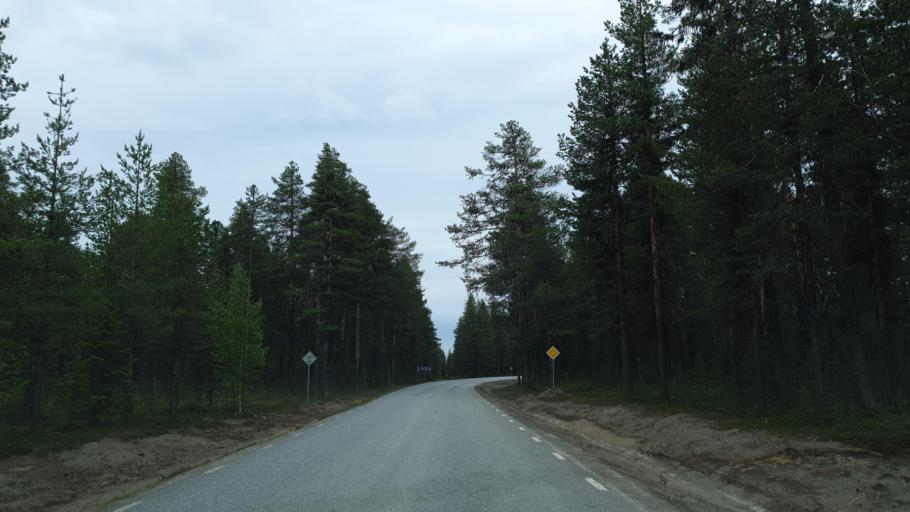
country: SE
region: Vaesterbotten
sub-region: Sorsele Kommun
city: Sorsele
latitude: 65.5518
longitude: 17.5081
